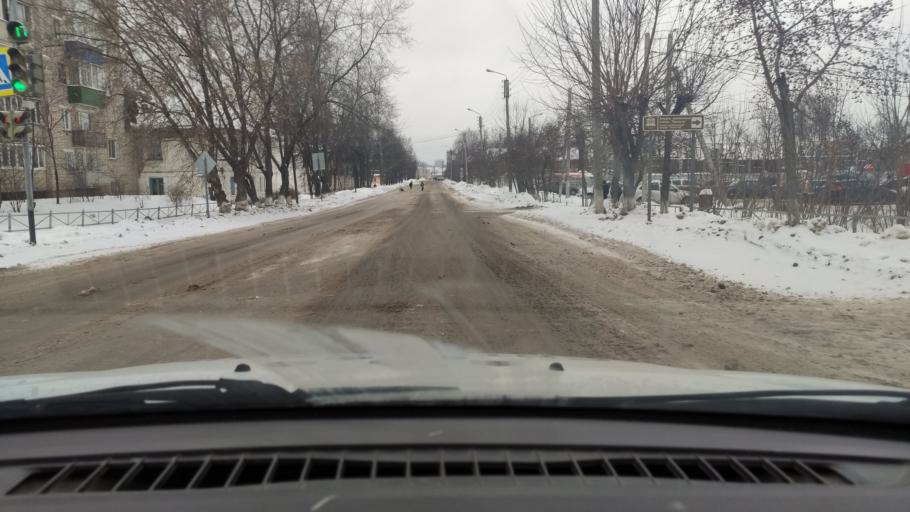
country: RU
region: Perm
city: Kungur
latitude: 57.4382
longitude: 56.9320
